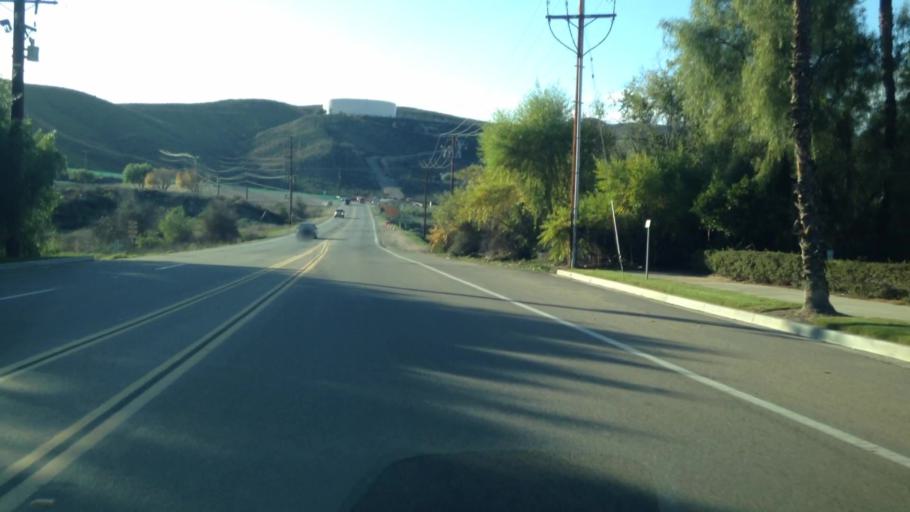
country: US
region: California
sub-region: Riverside County
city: Home Gardens
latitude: 33.8584
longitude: -117.4489
